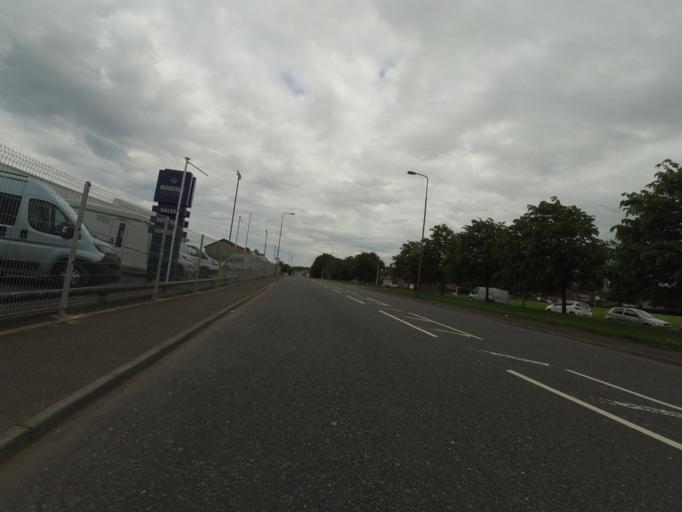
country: GB
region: Scotland
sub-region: East Lothian
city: Musselburgh
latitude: 55.9211
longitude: -3.0379
